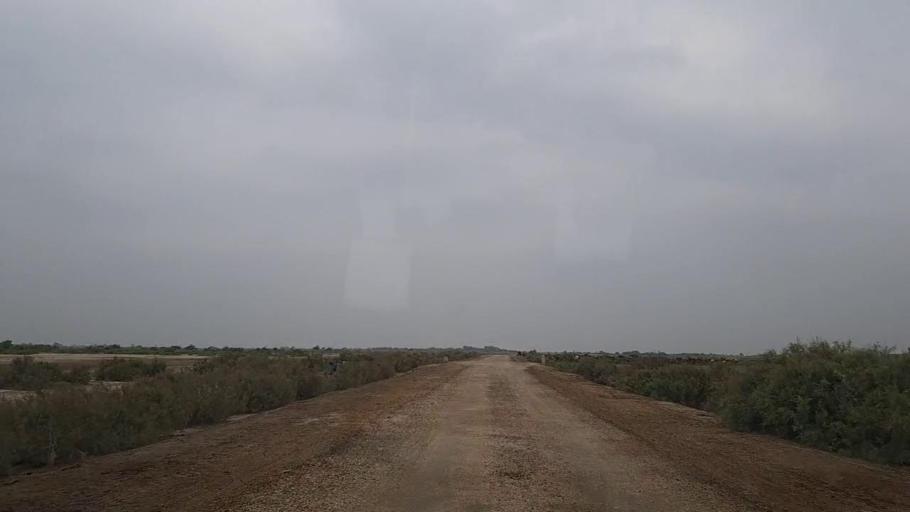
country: PK
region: Sindh
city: Mirpur Sakro
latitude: 24.6277
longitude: 67.7190
